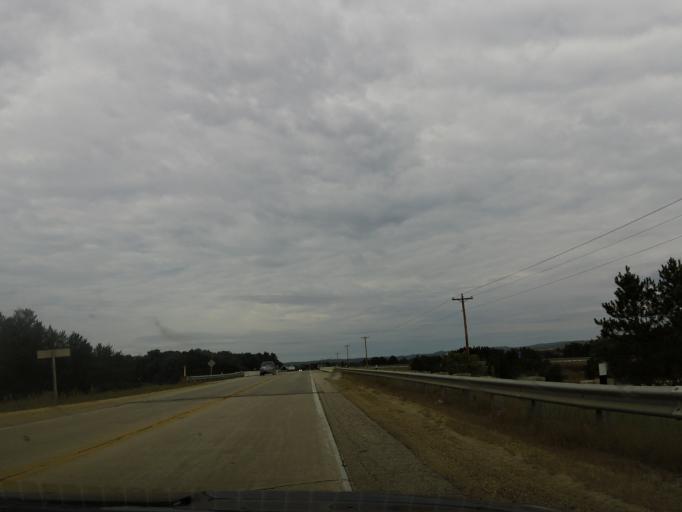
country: US
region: Wisconsin
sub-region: Monroe County
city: Sparta
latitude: 43.9414
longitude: -90.7629
